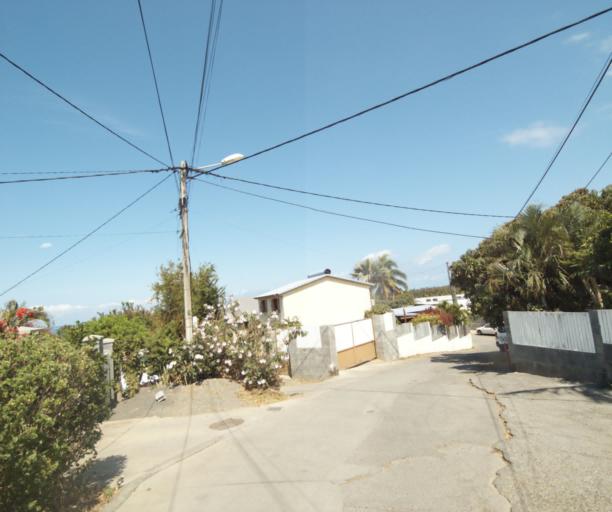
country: RE
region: Reunion
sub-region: Reunion
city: Trois-Bassins
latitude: -21.0937
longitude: 55.2412
